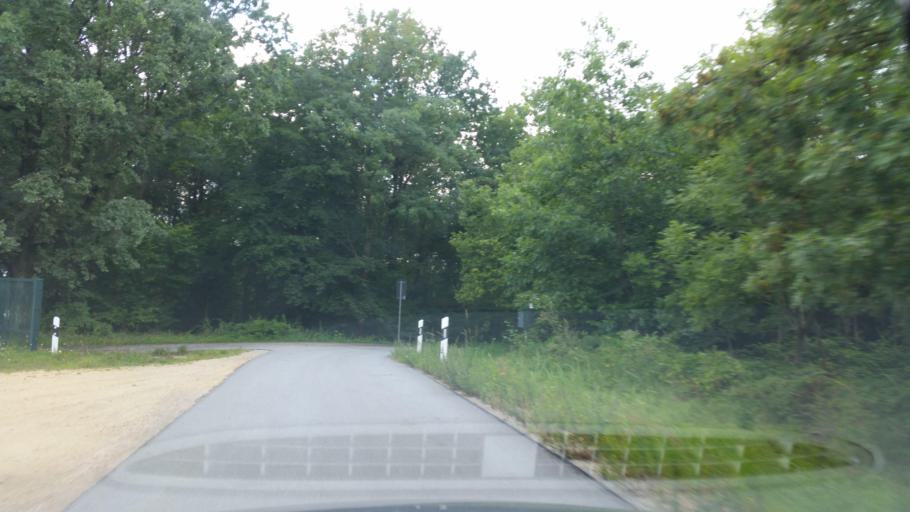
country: DE
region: Saxony
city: Sohland am Rotstein
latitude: 51.1123
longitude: 14.7547
